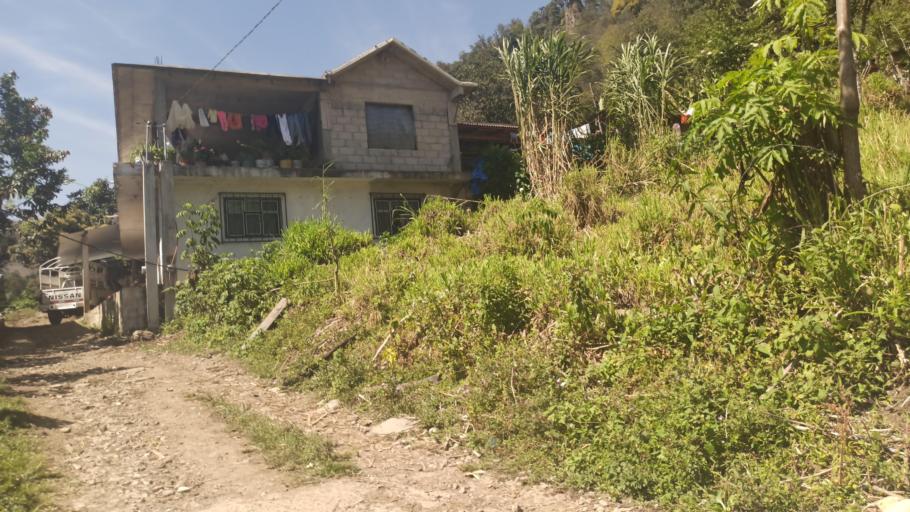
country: MX
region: Veracruz
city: Xocotla
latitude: 18.9827
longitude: -97.0878
